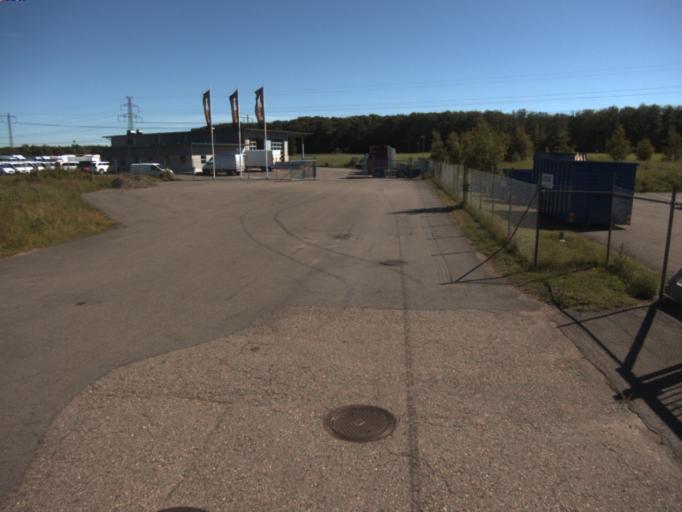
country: SE
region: Skane
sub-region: Helsingborg
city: Odakra
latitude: 56.0914
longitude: 12.7413
